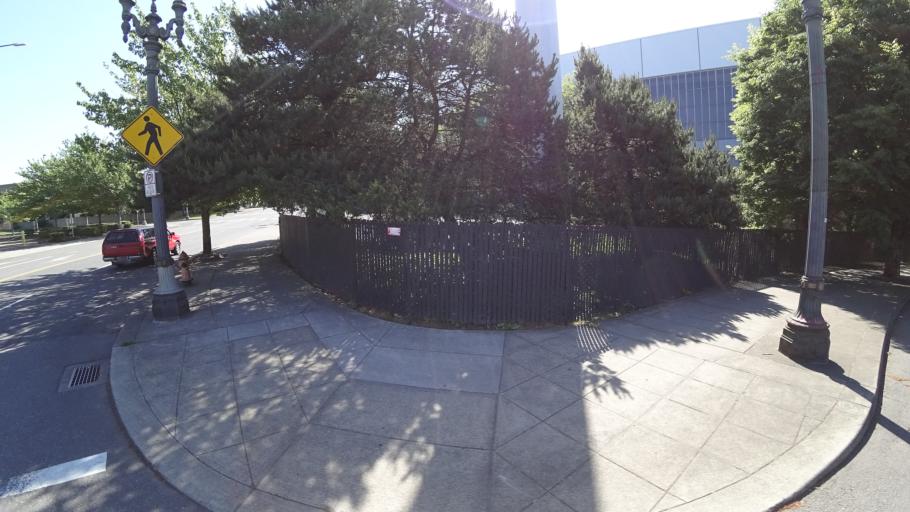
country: US
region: Oregon
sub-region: Multnomah County
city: Portland
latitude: 45.5329
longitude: -122.6705
